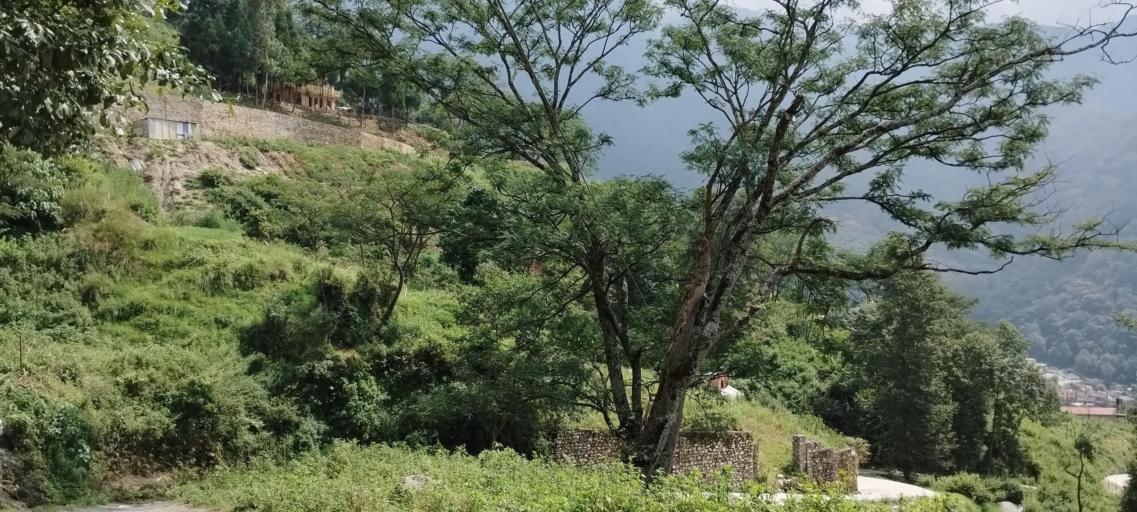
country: NP
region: Central Region
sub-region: Bagmati Zone
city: Kathmandu
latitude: 27.7907
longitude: 85.3631
